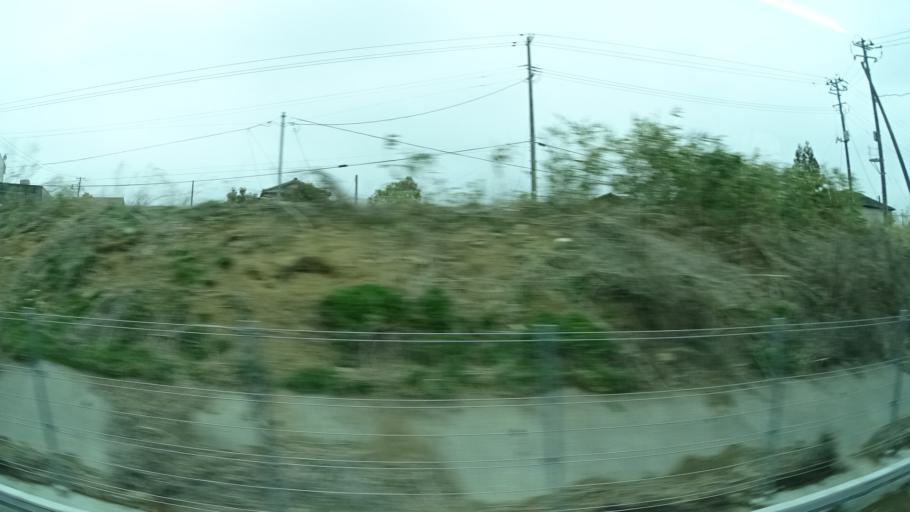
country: JP
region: Fukushima
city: Namie
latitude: 37.4032
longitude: 140.9852
